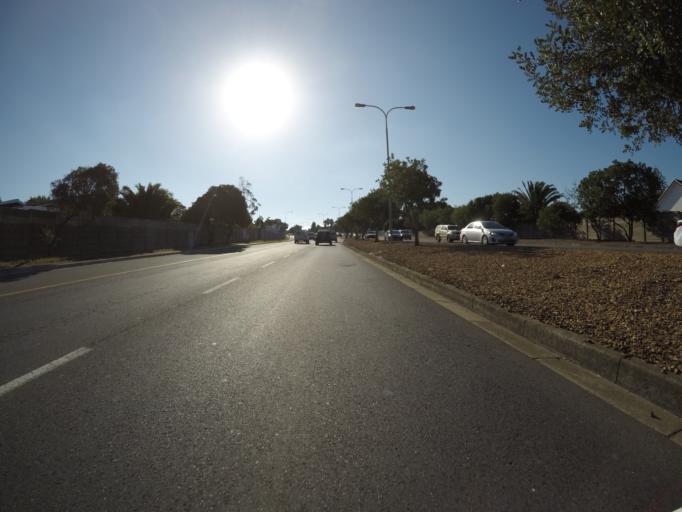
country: ZA
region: Western Cape
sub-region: City of Cape Town
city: Kraaifontein
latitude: -33.8726
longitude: 18.6509
